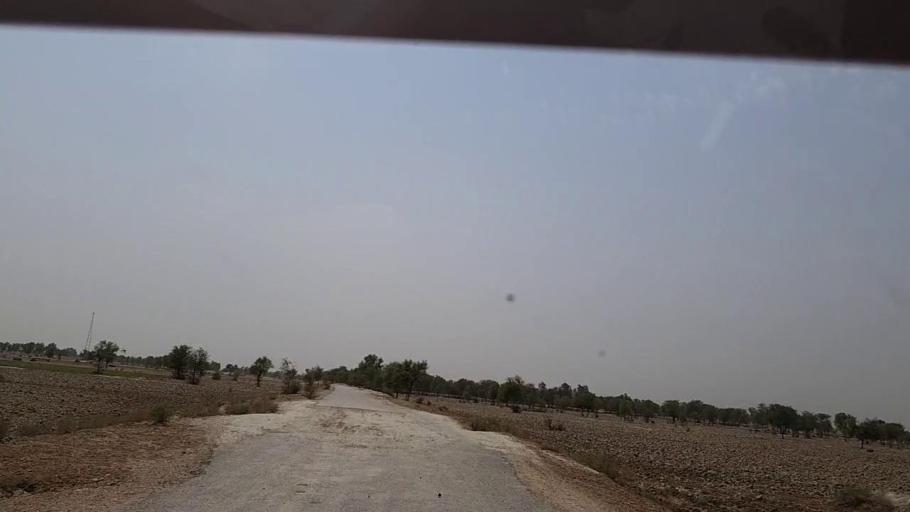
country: PK
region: Sindh
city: Khairpur Nathan Shah
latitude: 27.0169
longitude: 67.5971
